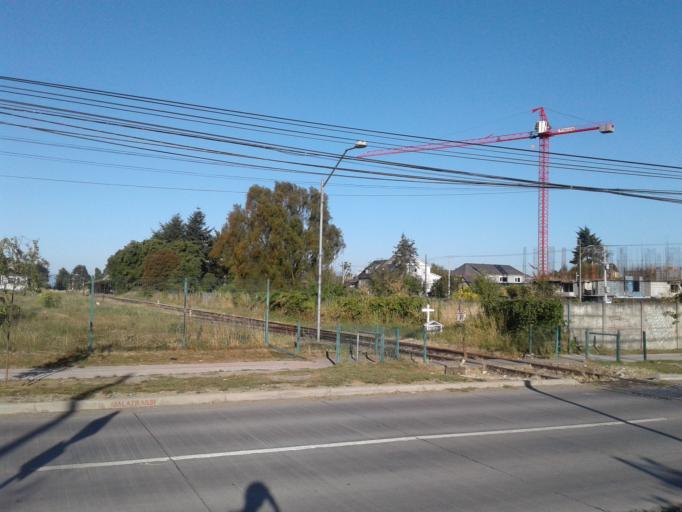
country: CL
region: Los Lagos
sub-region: Provincia de Llanquihue
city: Puerto Varas
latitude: -41.3202
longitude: -72.9902
